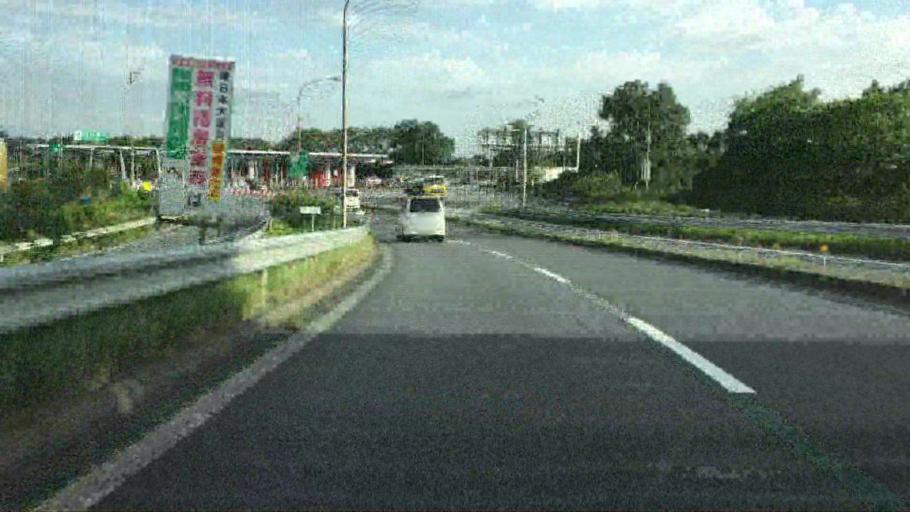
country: JP
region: Tochigi
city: Sano
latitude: 36.2949
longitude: 139.6155
